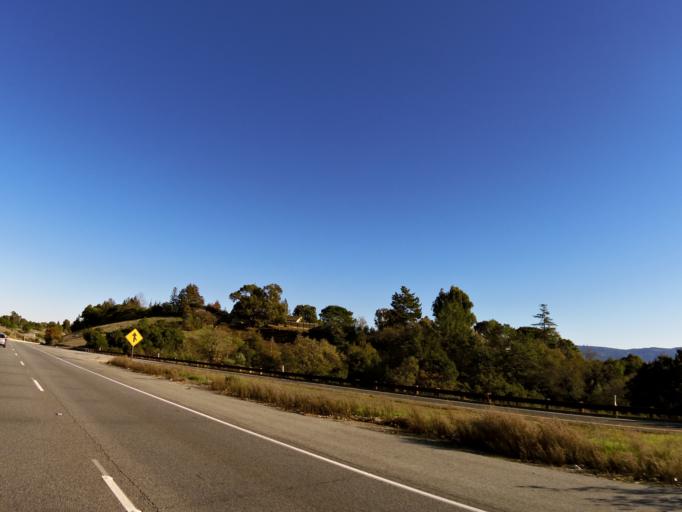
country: US
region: California
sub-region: San Mateo County
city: Woodside
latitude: 37.4438
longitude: -122.2618
